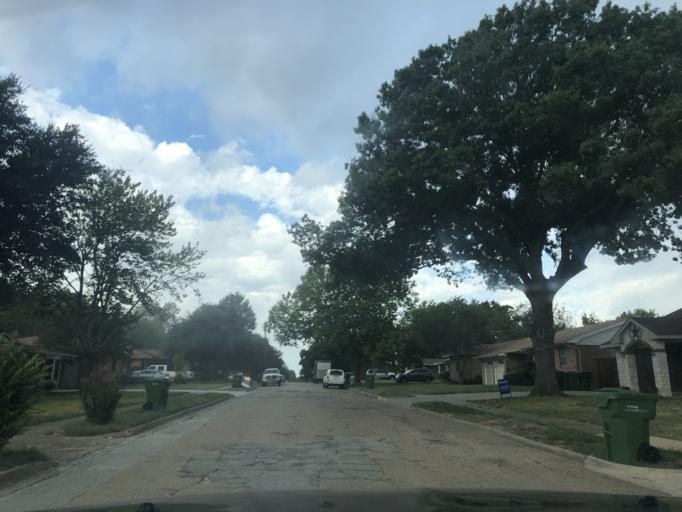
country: US
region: Texas
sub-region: Dallas County
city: Garland
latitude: 32.8771
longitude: -96.6493
